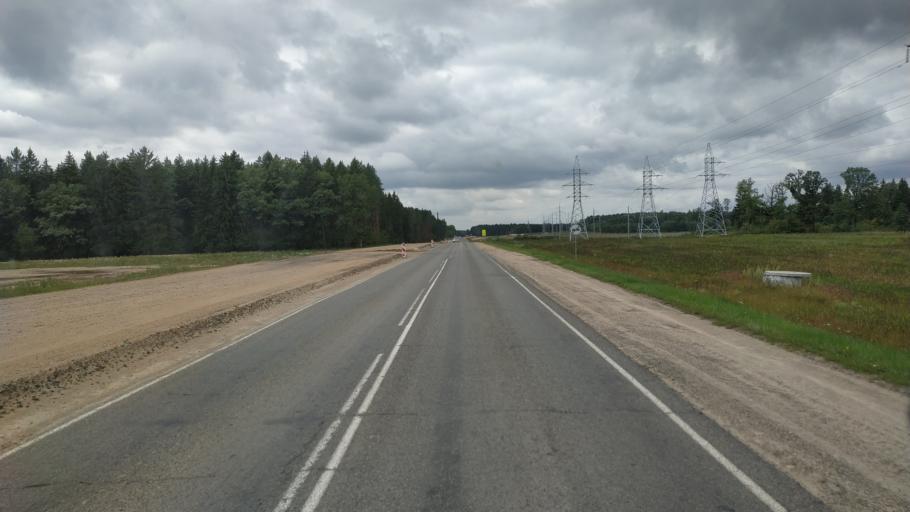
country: BY
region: Mogilev
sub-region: Mahilyowski Rayon
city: Veyno
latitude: 53.8729
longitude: 30.4463
